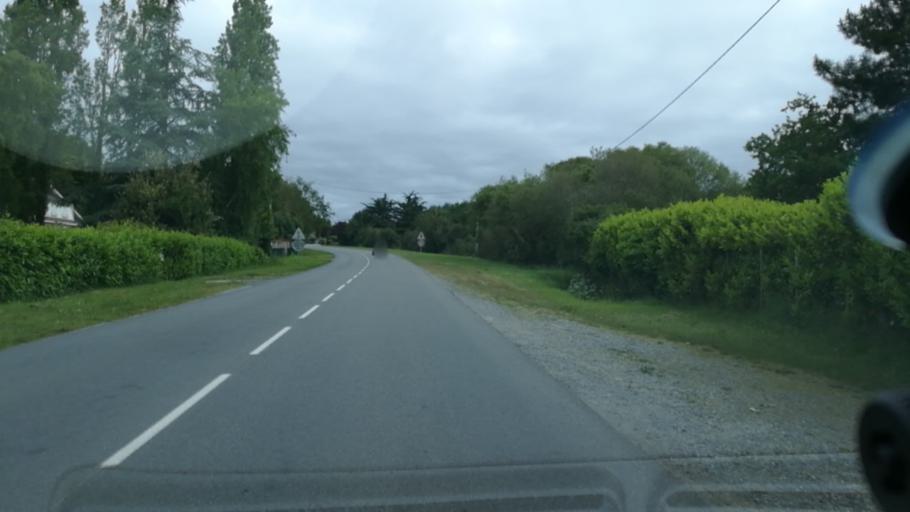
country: FR
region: Brittany
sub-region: Departement du Morbihan
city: Penestin
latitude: 47.4709
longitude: -2.4786
